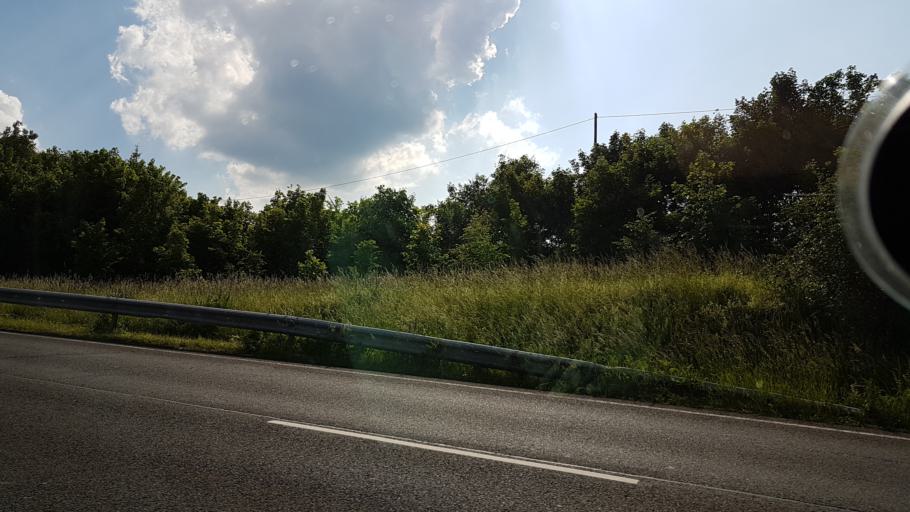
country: DE
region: Rheinland-Pfalz
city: Fohren-Linden
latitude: 49.5752
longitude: 7.2862
